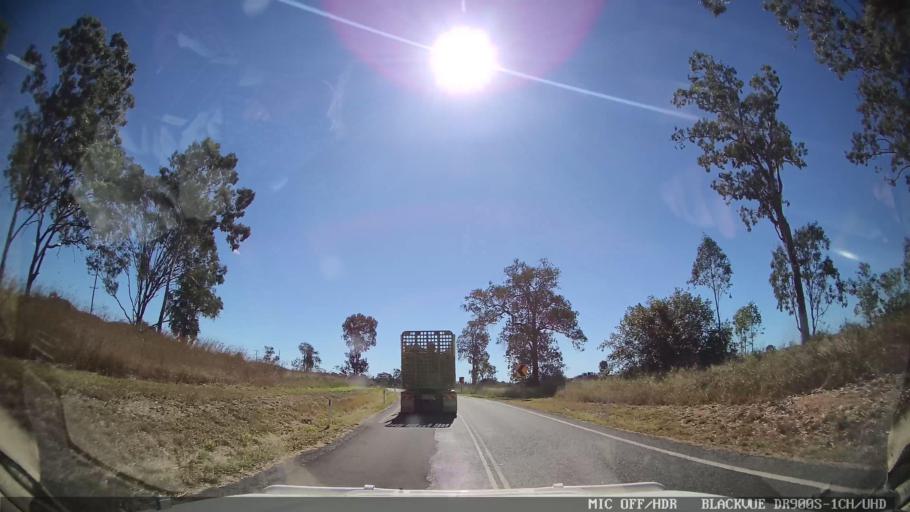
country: AU
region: Queensland
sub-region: Gladstone
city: Toolooa
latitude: -24.2732
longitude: 151.2760
